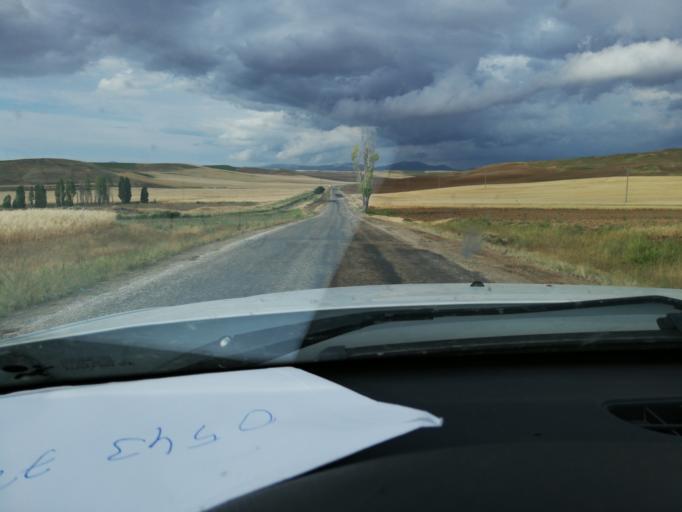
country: TR
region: Kirsehir
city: Kirsehir
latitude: 39.0359
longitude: 34.1445
